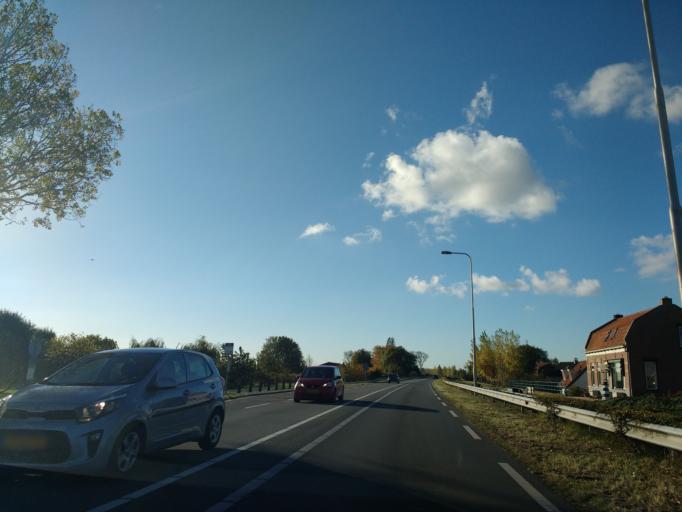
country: NL
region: Zeeland
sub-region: Gemeente Vlissingen
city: Vlissingen
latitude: 51.3784
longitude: 3.5481
